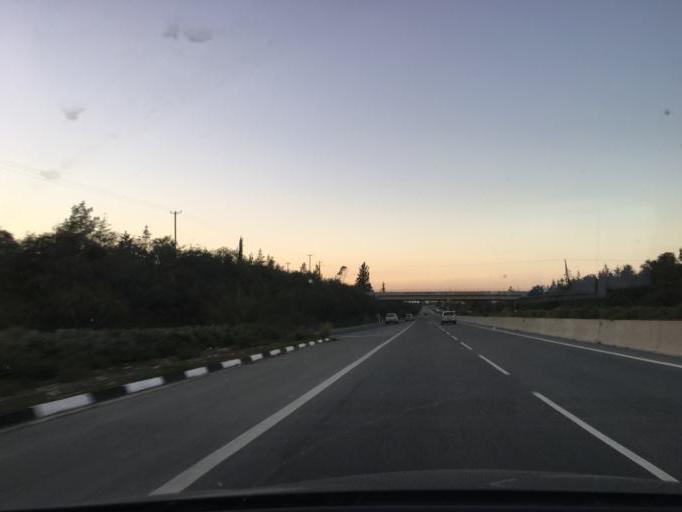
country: CY
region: Larnaka
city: Dhromolaxia
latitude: 34.8889
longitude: 33.5861
